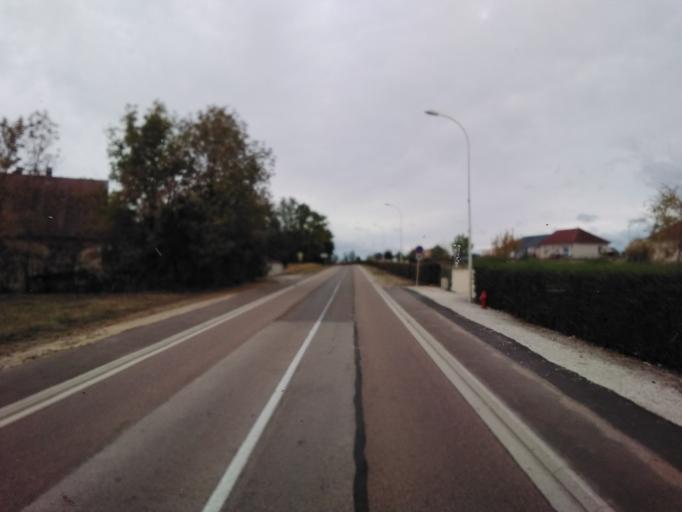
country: FR
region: Champagne-Ardenne
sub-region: Departement de l'Aube
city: Vendeuvre-sur-Barse
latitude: 48.2311
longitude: 4.4597
